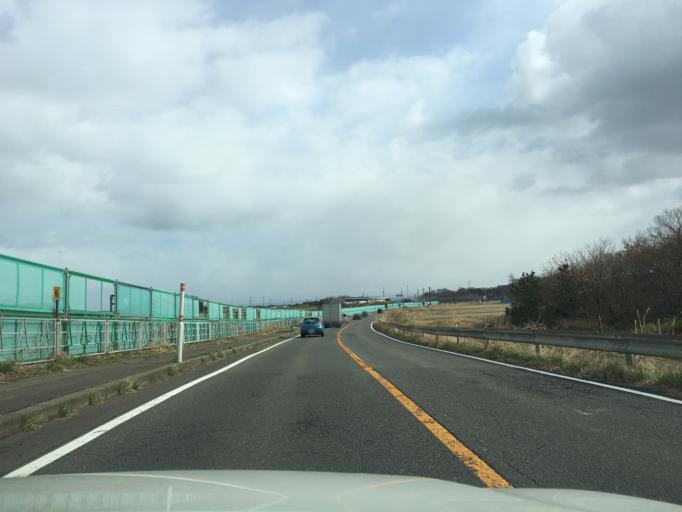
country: JP
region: Yamagata
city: Yuza
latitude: 39.2751
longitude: 139.9251
